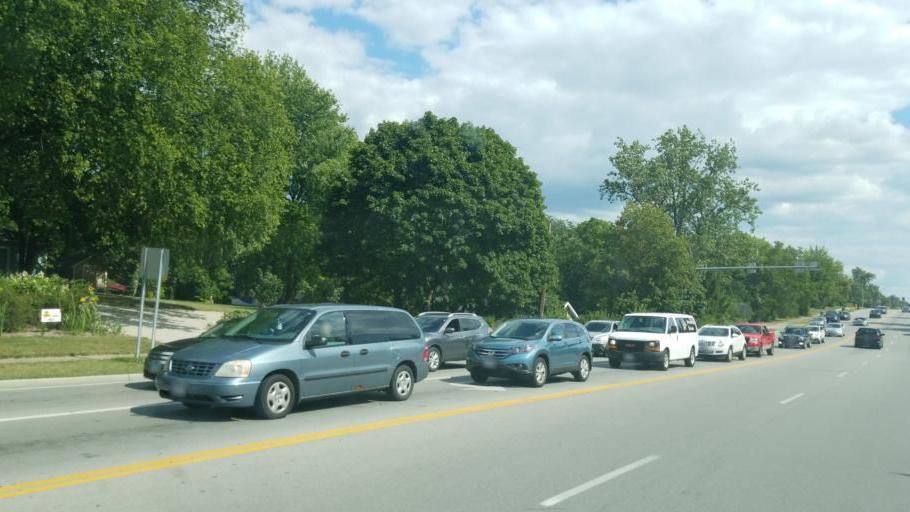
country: US
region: Ohio
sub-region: Lucas County
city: Maumee
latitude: 41.5558
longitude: -83.6417
